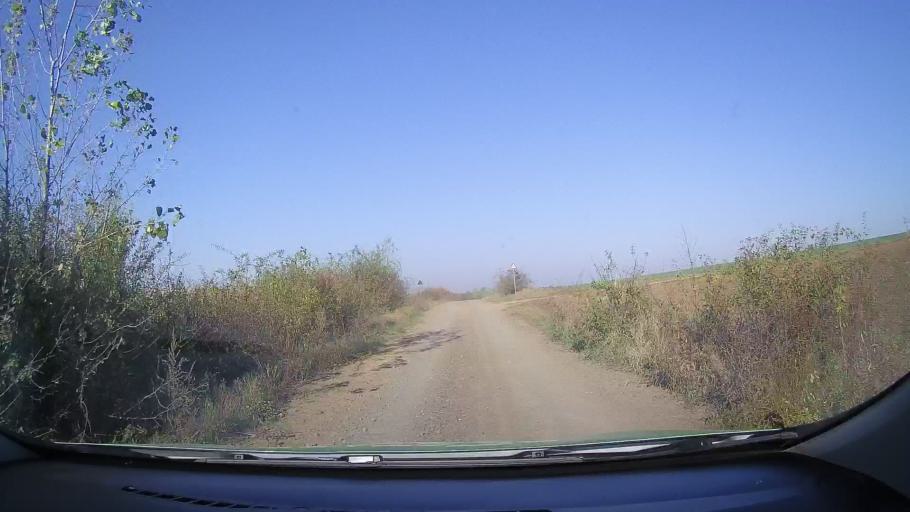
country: RO
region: Satu Mare
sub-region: Comuna Sauca
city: Sauca
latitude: 47.4813
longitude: 22.4679
